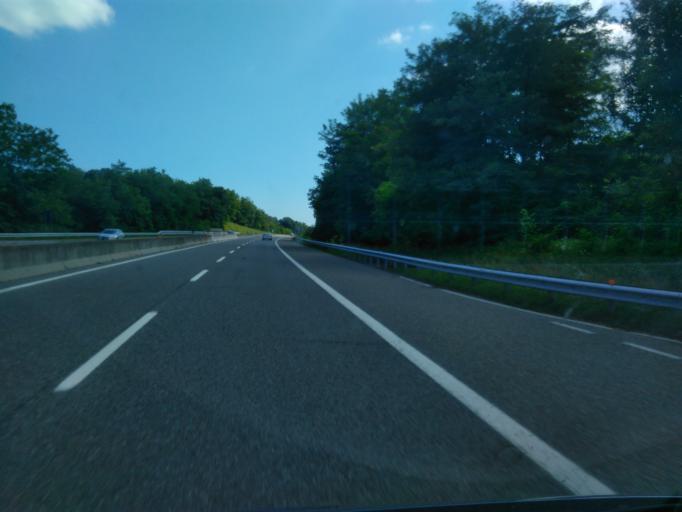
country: IT
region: Piedmont
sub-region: Provincia di Novara
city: Paruzzaro
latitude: 45.7549
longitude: 8.5028
